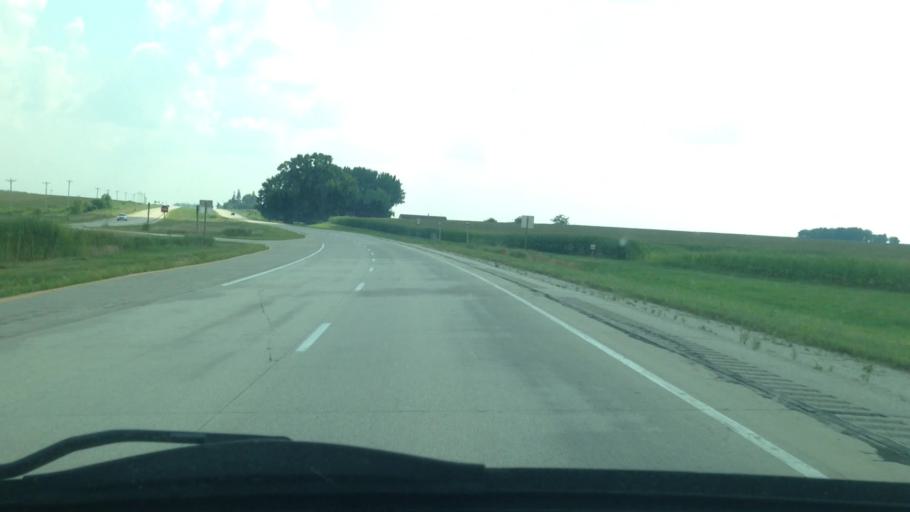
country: US
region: Iowa
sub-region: Bremer County
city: Tripoli
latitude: 42.8853
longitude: -92.3370
